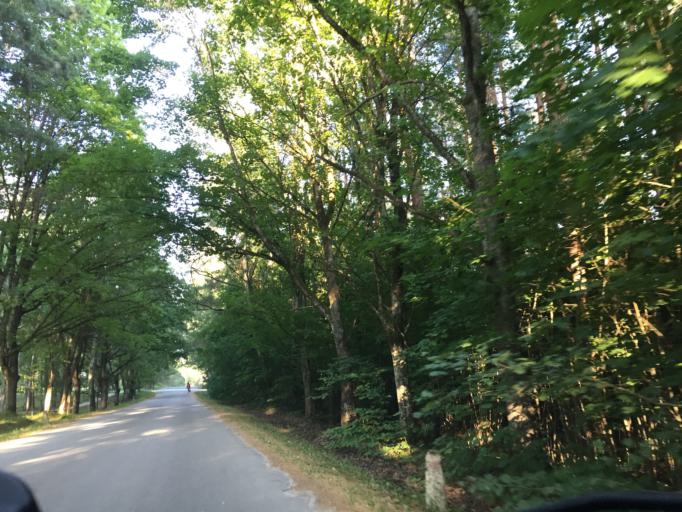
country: LV
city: Tervete
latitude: 56.4799
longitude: 23.3731
